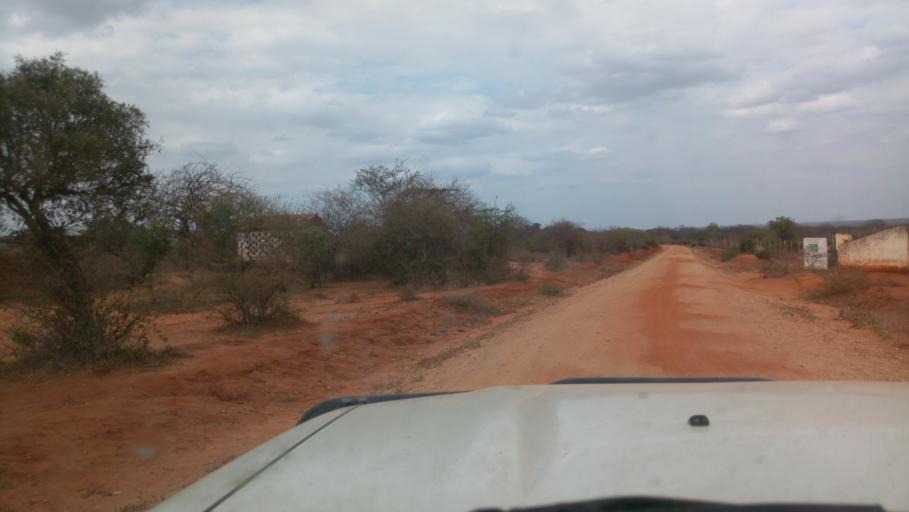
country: KE
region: Kitui
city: Kitui
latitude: -1.7963
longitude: 38.4278
